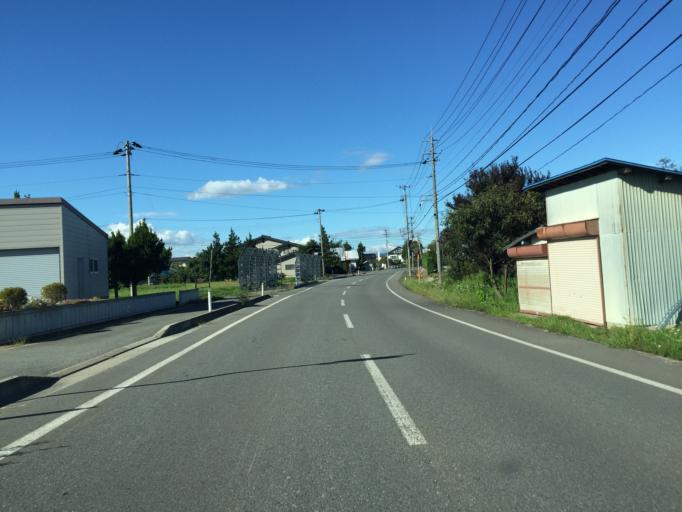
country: JP
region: Yamagata
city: Yonezawa
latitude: 37.9534
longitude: 140.1085
